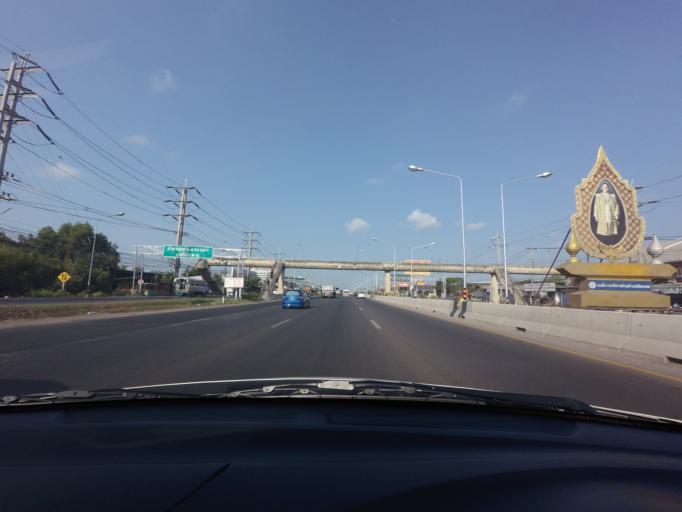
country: TH
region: Samut Sakhon
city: Samut Sakhon
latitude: 13.5242
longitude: 100.1839
